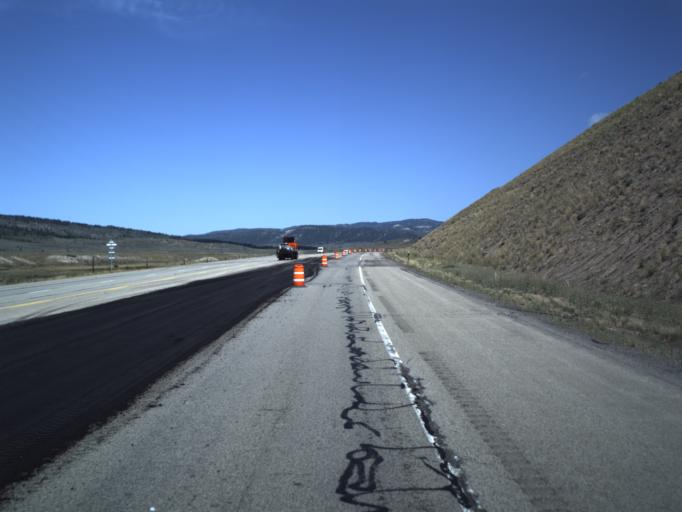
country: US
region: Utah
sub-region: Carbon County
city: Helper
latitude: 39.8646
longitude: -111.0287
